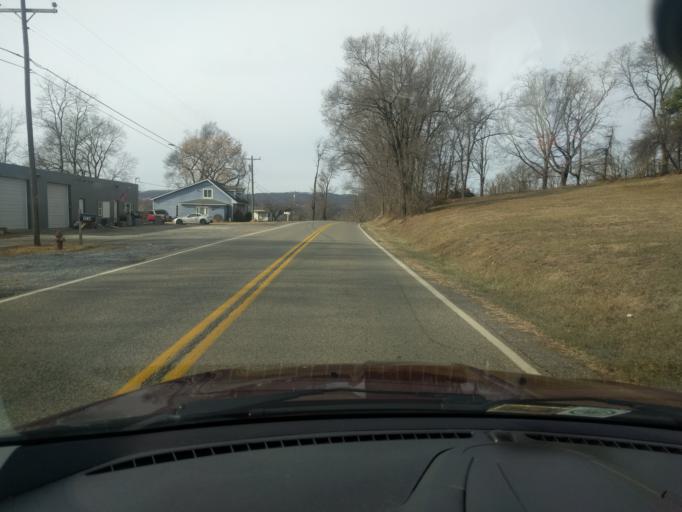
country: US
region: Virginia
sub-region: Augusta County
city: Stuarts Draft
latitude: 38.0412
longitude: -79.0823
